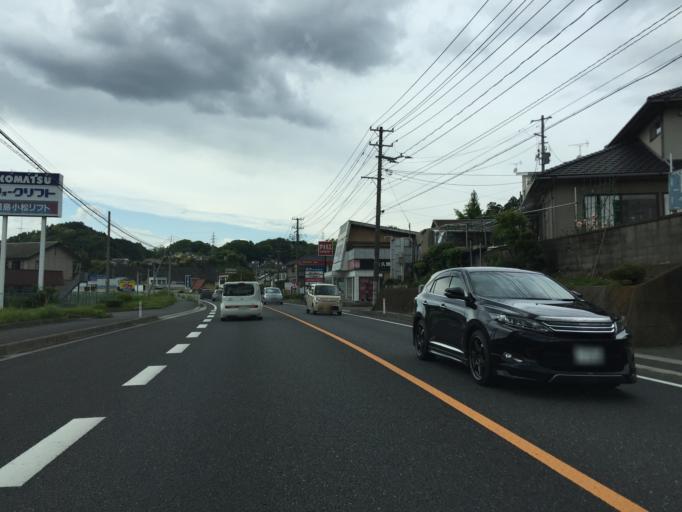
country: JP
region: Fukushima
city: Iwaki
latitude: 36.9981
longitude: 140.8598
